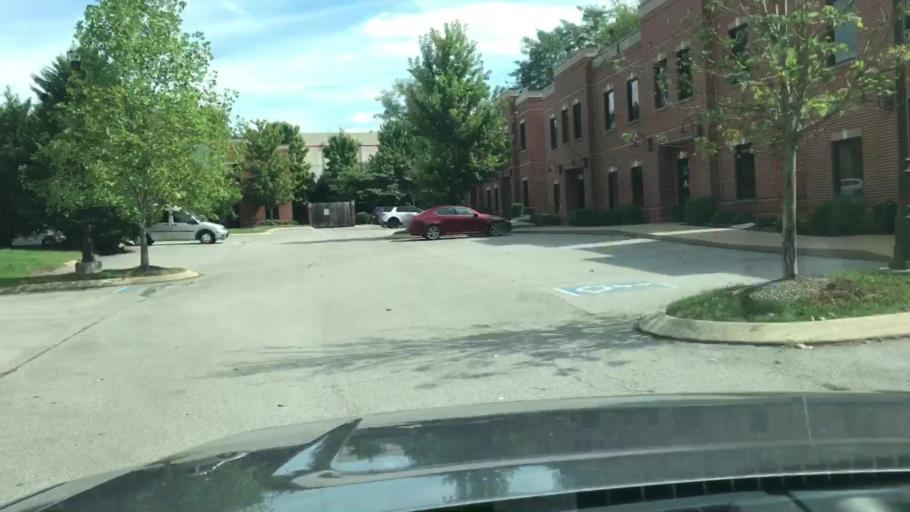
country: US
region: Tennessee
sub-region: Williamson County
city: Franklin
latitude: 35.9388
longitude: -86.8329
